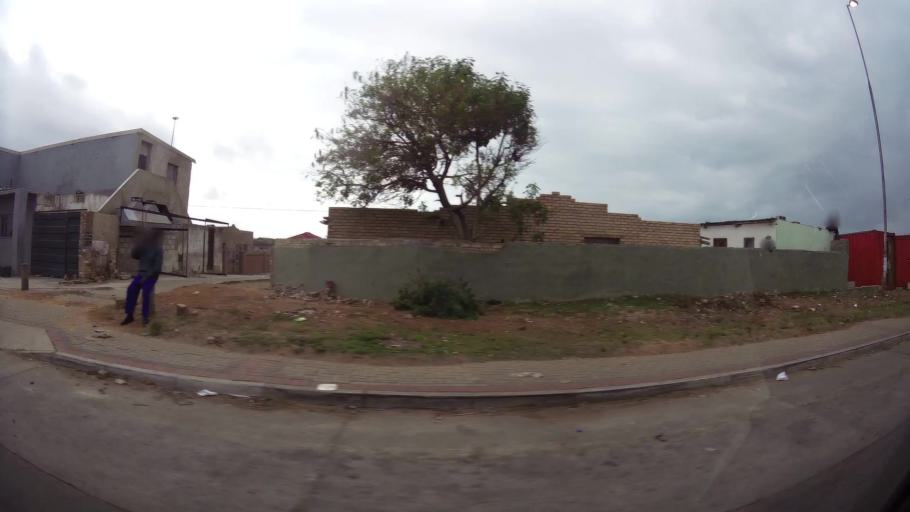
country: ZA
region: Eastern Cape
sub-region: Nelson Mandela Bay Metropolitan Municipality
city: Port Elizabeth
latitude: -33.8882
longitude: 25.5867
